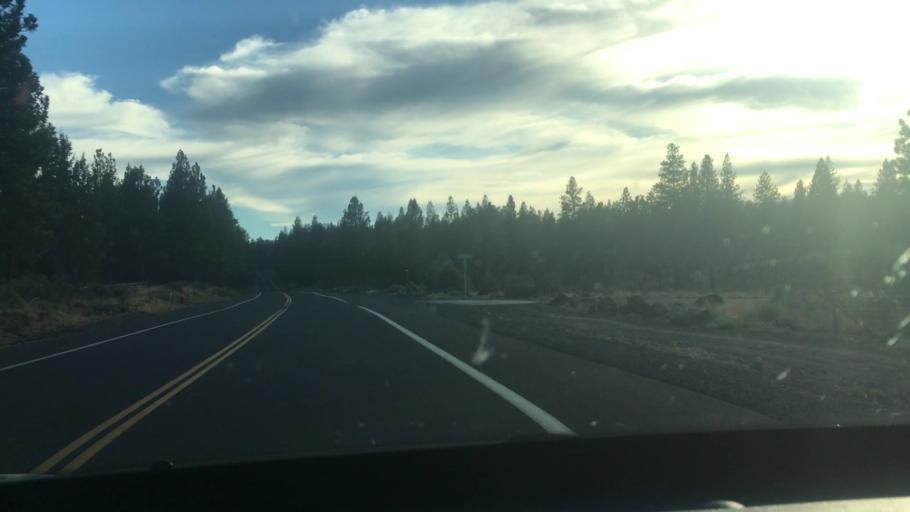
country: US
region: Oregon
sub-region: Deschutes County
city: Bend
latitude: 44.0518
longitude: -121.3775
